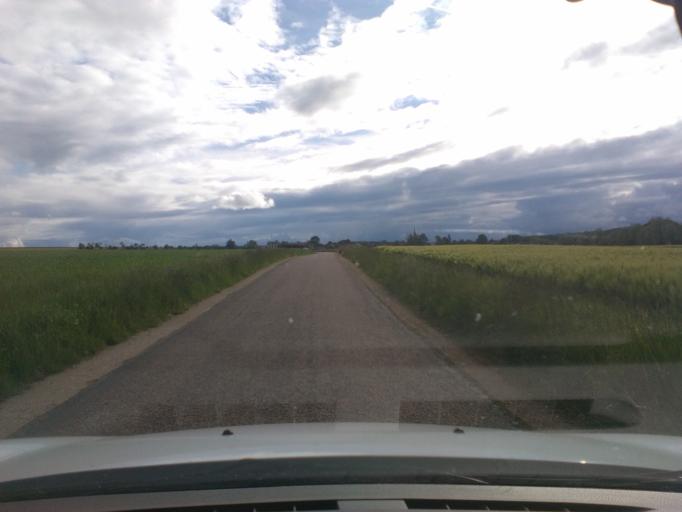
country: FR
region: Lorraine
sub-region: Departement des Vosges
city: Mirecourt
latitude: 48.3341
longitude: 6.0727
